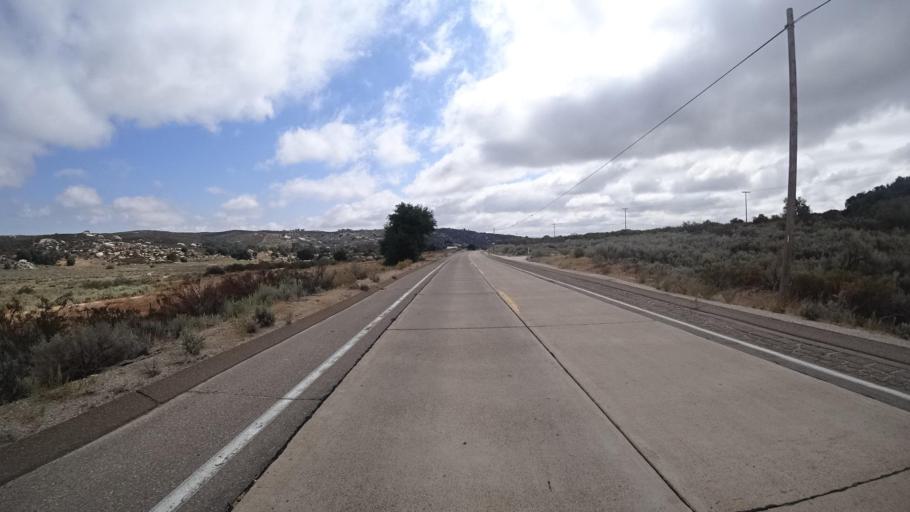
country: US
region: California
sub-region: San Diego County
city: Campo
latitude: 32.6938
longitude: -116.3436
